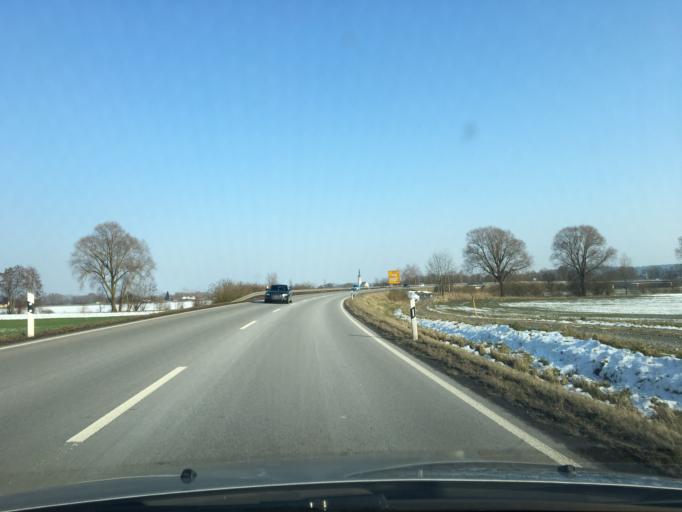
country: DE
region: Bavaria
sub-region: Lower Bavaria
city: Frontenhausen
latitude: 48.5556
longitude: 12.5365
